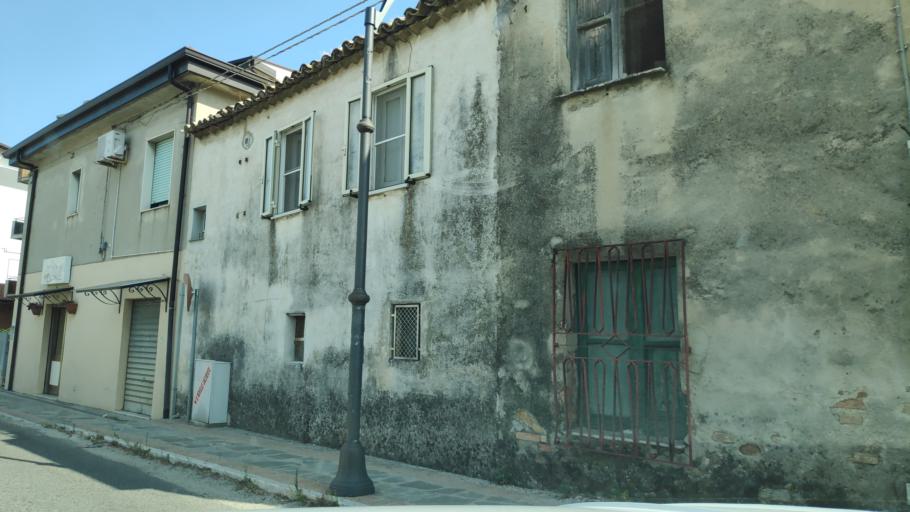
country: IT
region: Calabria
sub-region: Provincia di Catanzaro
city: Marina di Davoli
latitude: 38.6675
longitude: 16.5435
